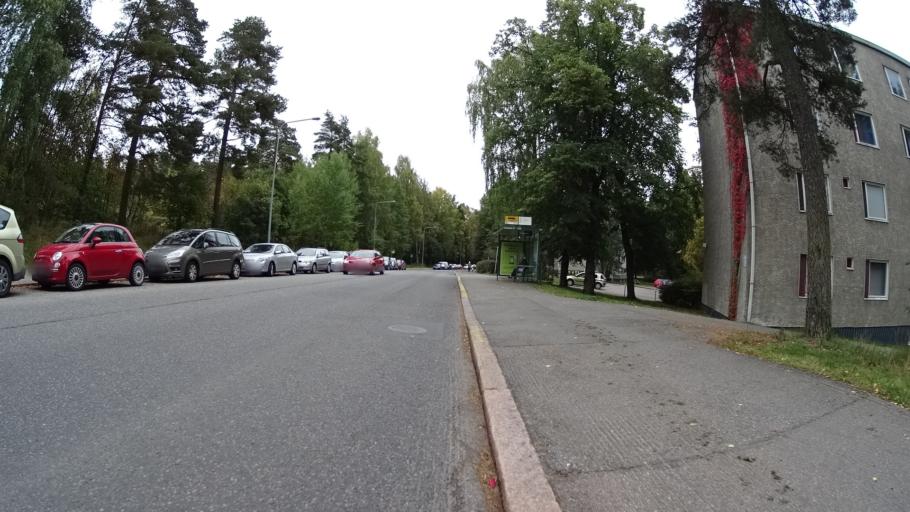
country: FI
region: Uusimaa
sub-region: Helsinki
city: Teekkarikylae
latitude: 60.2092
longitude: 24.8743
